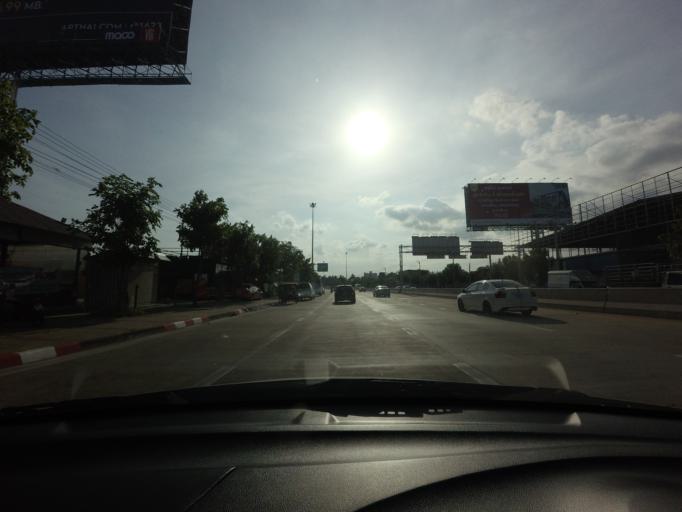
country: TH
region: Samut Prakan
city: Phra Pradaeng
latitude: 13.6649
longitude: 100.5232
